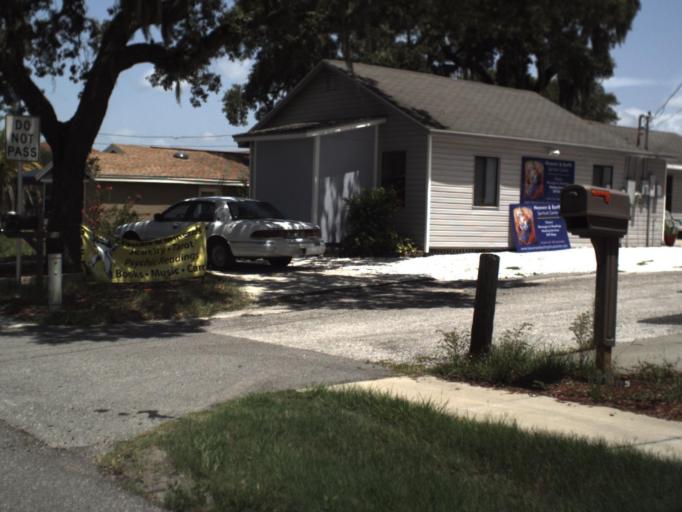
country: US
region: Florida
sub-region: Pinellas County
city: Palm Harbor
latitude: 28.0803
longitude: -82.7672
